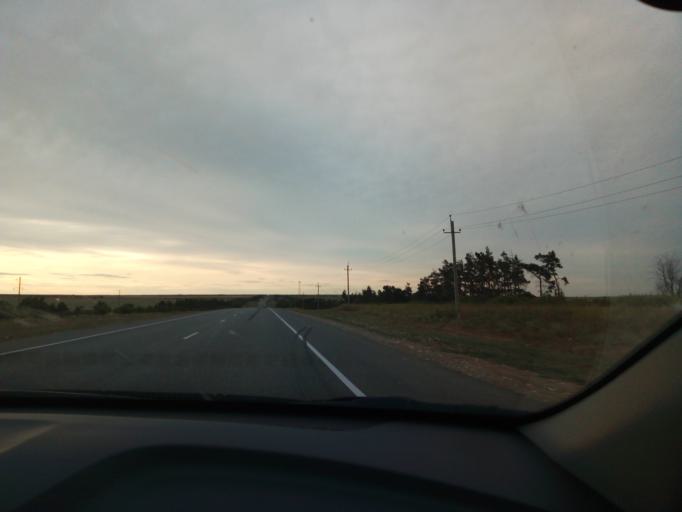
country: RU
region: Volgograd
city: Primorsk
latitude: 49.2548
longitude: 44.8863
